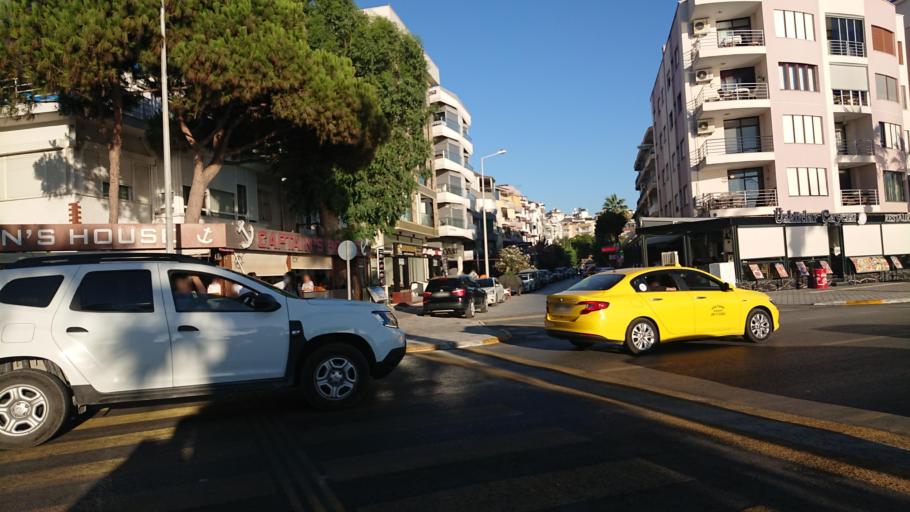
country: TR
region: Aydin
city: Kusadasi
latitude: 37.8654
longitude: 27.2627
